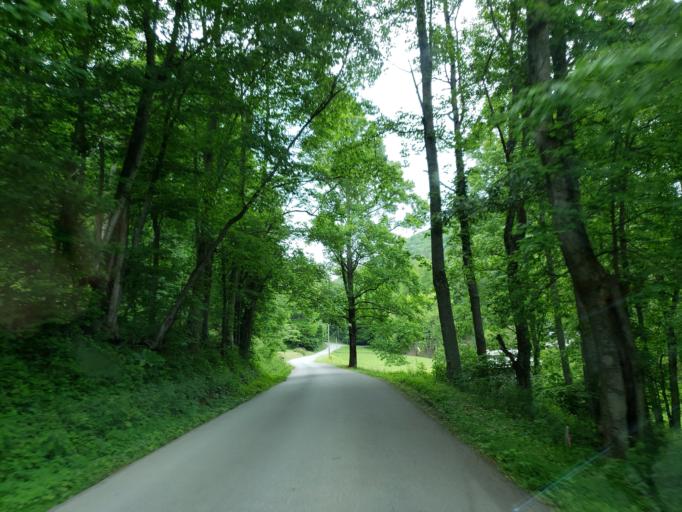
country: US
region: Georgia
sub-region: Fannin County
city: Blue Ridge
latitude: 34.8346
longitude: -84.4110
